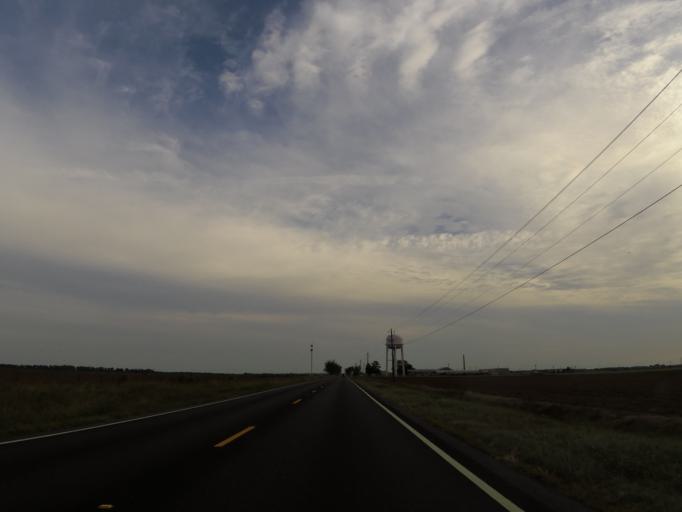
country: US
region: Alabama
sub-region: Escambia County
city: Atmore
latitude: 31.1644
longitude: -87.4638
